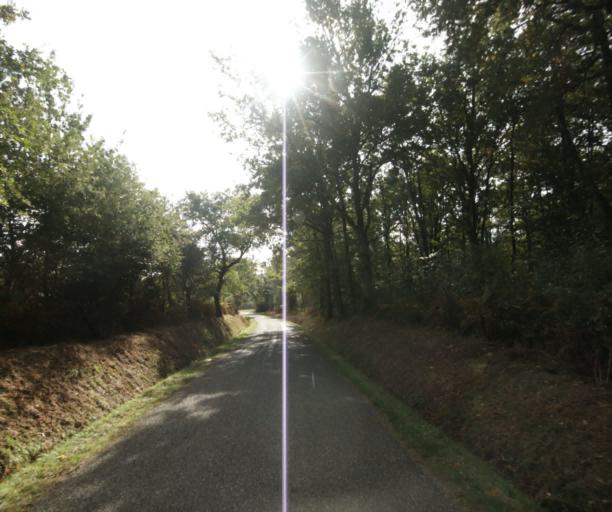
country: FR
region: Midi-Pyrenees
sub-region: Departement du Gers
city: Eauze
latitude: 43.9351
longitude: 0.1033
